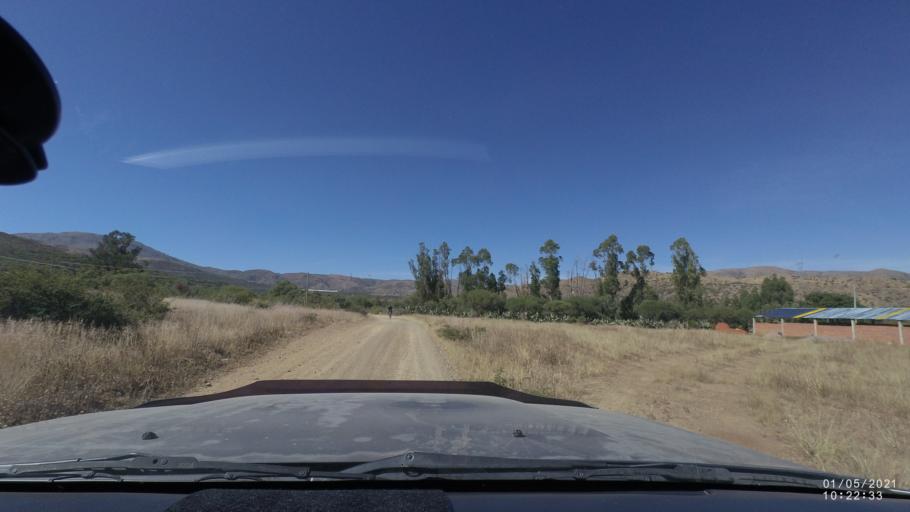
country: BO
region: Cochabamba
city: Capinota
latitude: -17.5690
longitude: -66.1989
